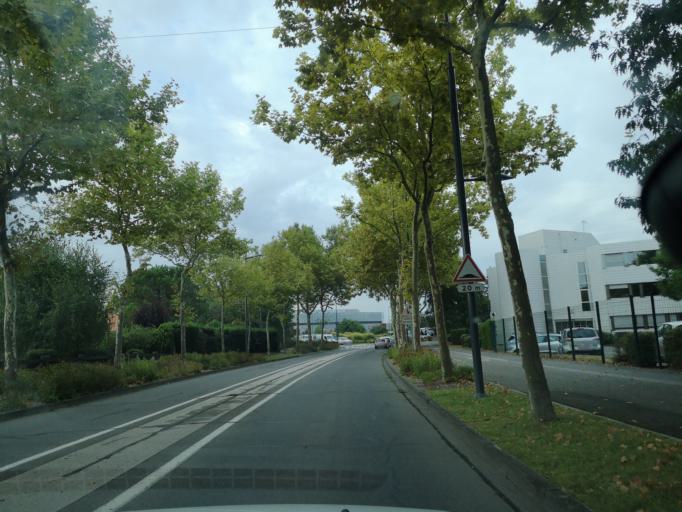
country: FR
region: Midi-Pyrenees
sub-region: Departement de la Haute-Garonne
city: Blagnac
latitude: 43.6278
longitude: 1.3861
